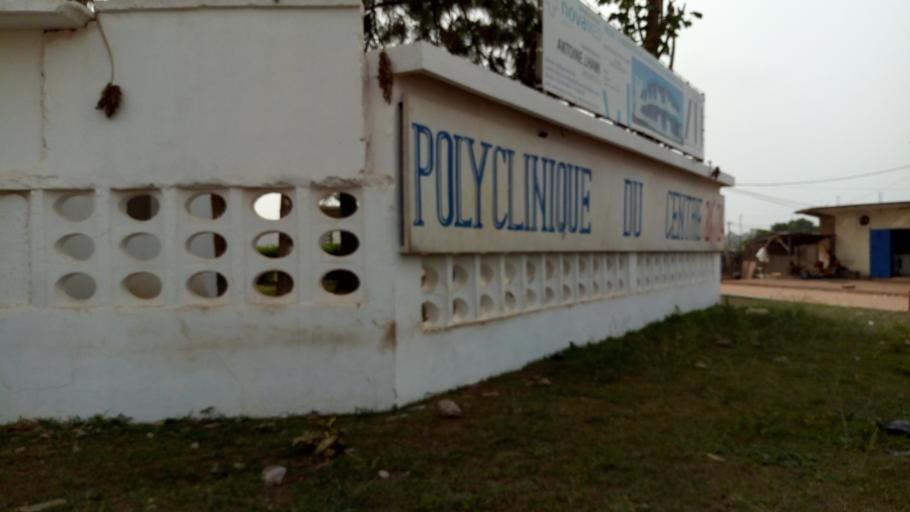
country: CI
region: Vallee du Bandama
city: Bouake
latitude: 7.7074
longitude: -5.0264
